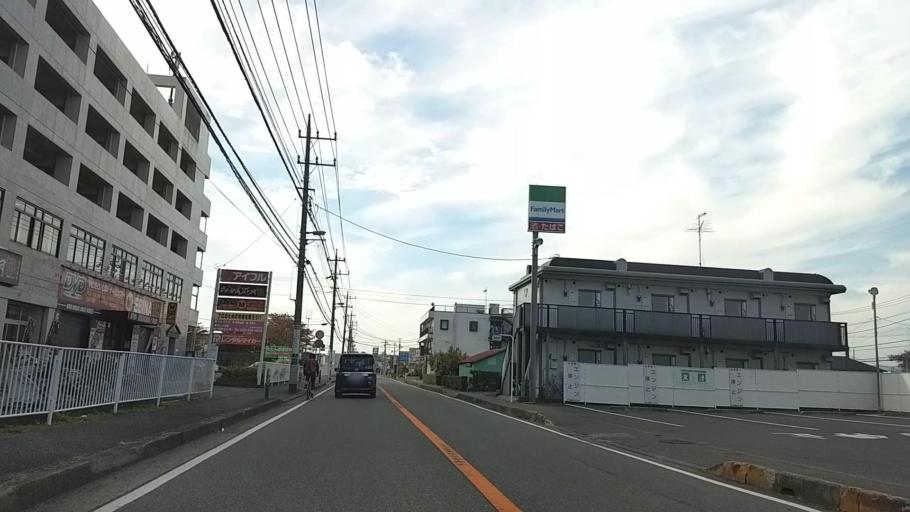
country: JP
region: Kanagawa
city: Zama
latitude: 35.4606
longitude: 139.3871
